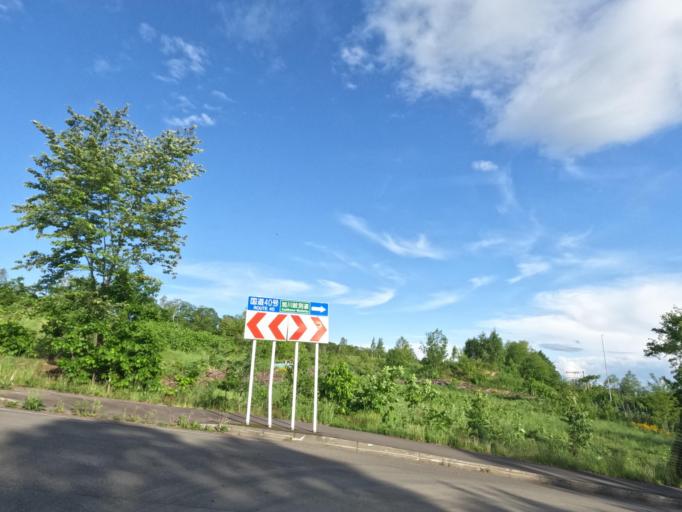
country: JP
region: Hokkaido
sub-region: Asahikawa-shi
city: Asahikawa
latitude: 43.9183
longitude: 142.5013
